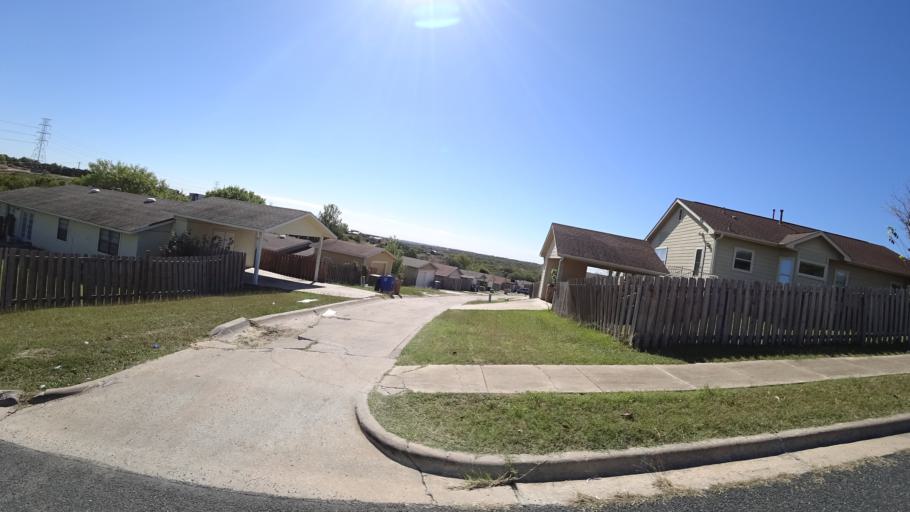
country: US
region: Texas
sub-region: Travis County
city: Hornsby Bend
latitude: 30.2891
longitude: -97.6446
